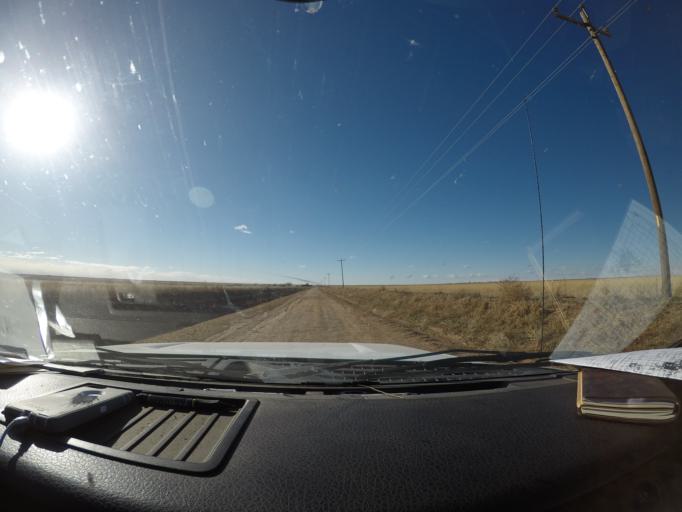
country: US
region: New Mexico
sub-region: Curry County
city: Clovis
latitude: 34.5648
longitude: -103.2498
